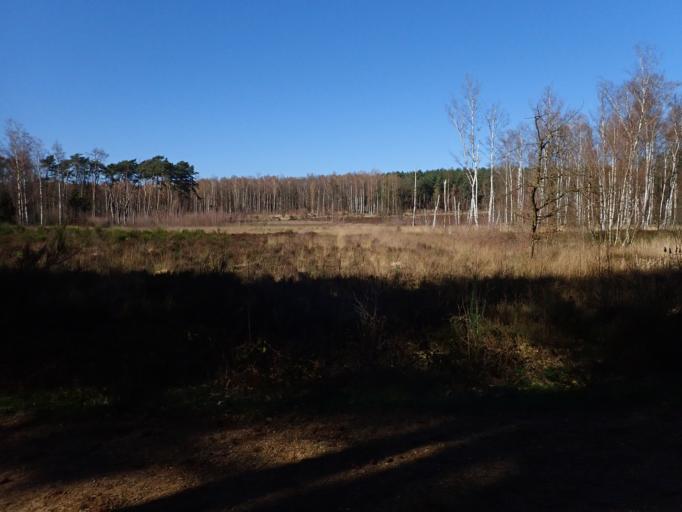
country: BE
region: Flanders
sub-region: Provincie Vlaams-Brabant
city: Scherpenheuvel-Zichem
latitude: 51.0341
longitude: 4.9979
